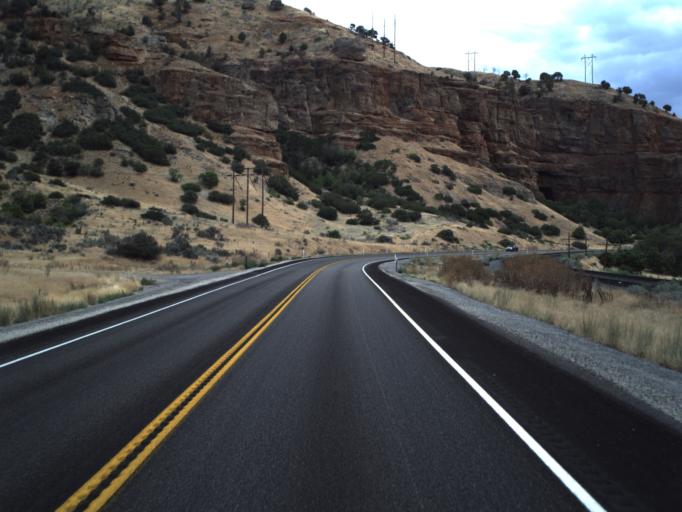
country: US
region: Utah
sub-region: Utah County
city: Mapleton
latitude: 39.9968
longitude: -111.4067
